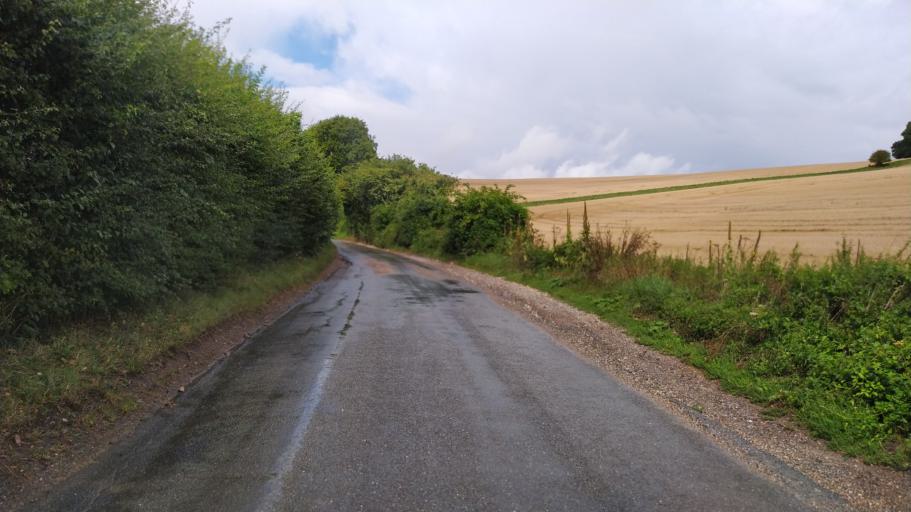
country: GB
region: England
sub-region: Hampshire
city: Swanmore
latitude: 51.0099
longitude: -1.1332
